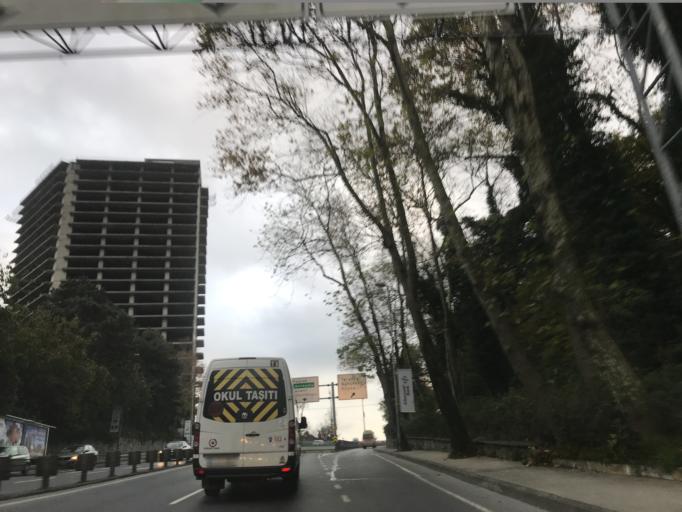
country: TR
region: Istanbul
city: Arikoey
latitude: 41.1426
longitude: 29.0284
